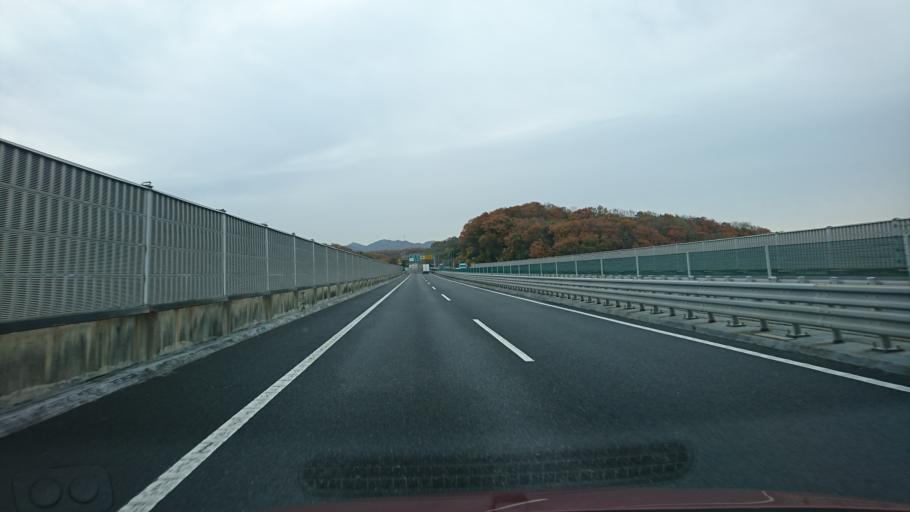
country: JP
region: Hyogo
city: Miki
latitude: 34.8005
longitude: 135.0469
